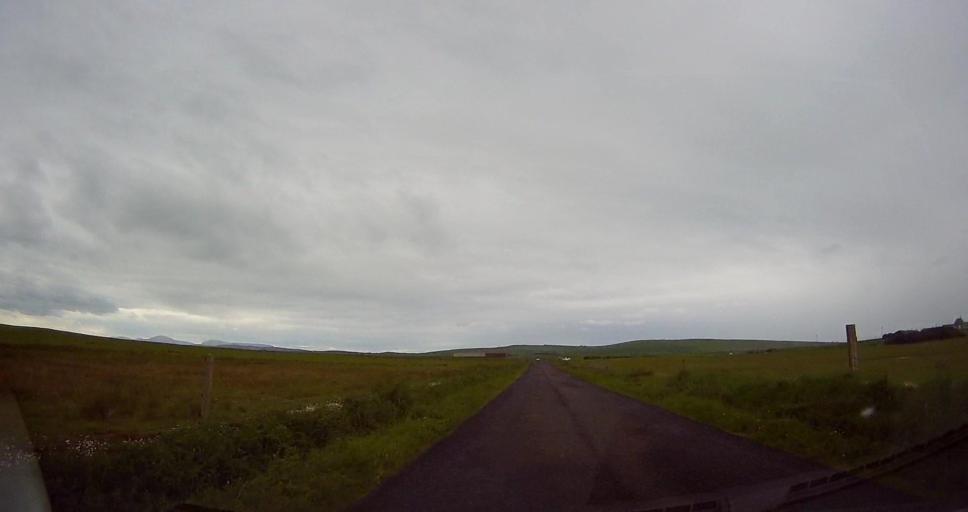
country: GB
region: Scotland
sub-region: Orkney Islands
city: Stromness
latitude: 59.1006
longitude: -3.2636
